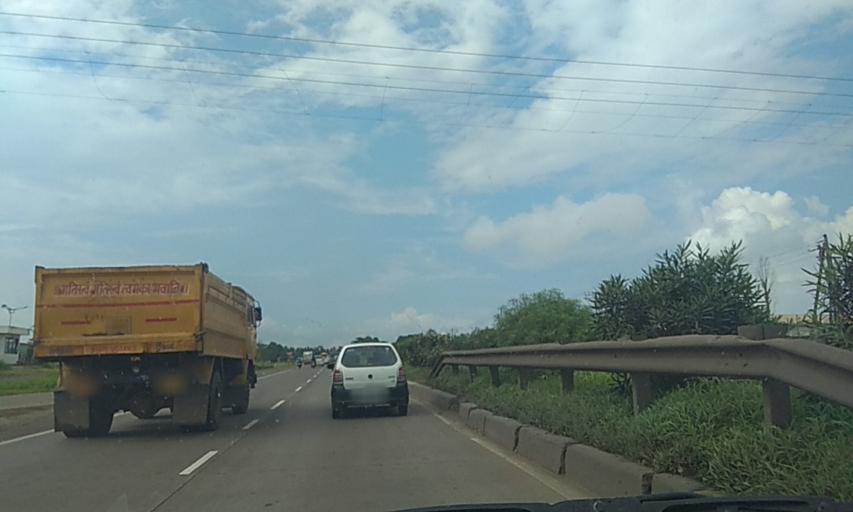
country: IN
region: Maharashtra
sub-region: Kolhapur
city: Kodoli
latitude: 16.8028
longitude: 74.2851
